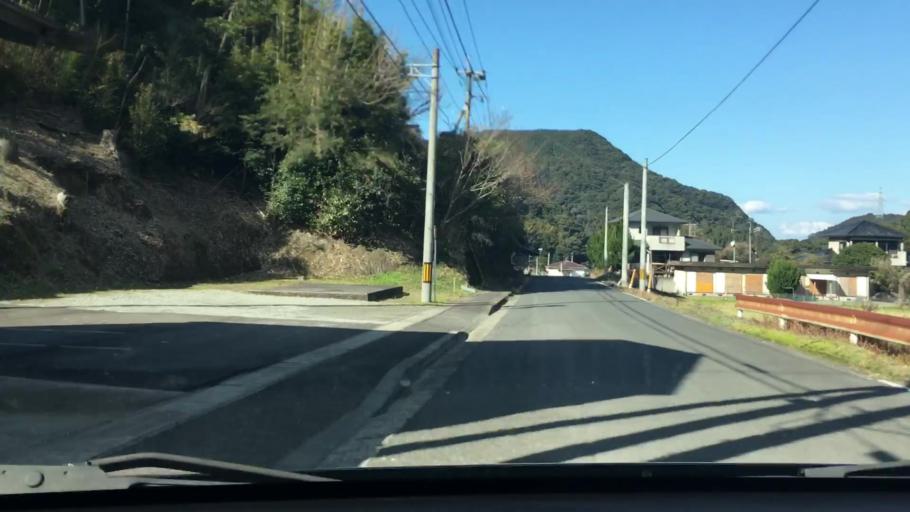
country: JP
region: Kagoshima
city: Ijuin
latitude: 31.7384
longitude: 130.4111
